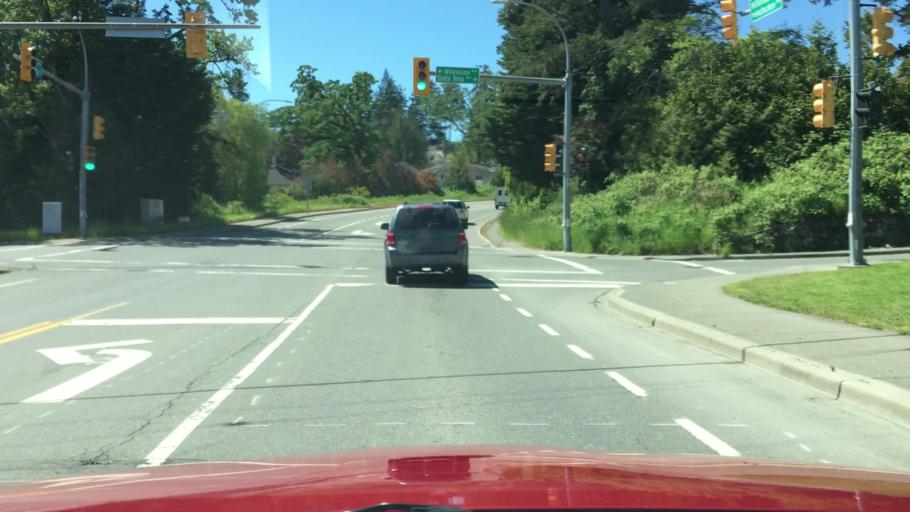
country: CA
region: British Columbia
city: Victoria
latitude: 48.4752
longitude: -123.4128
